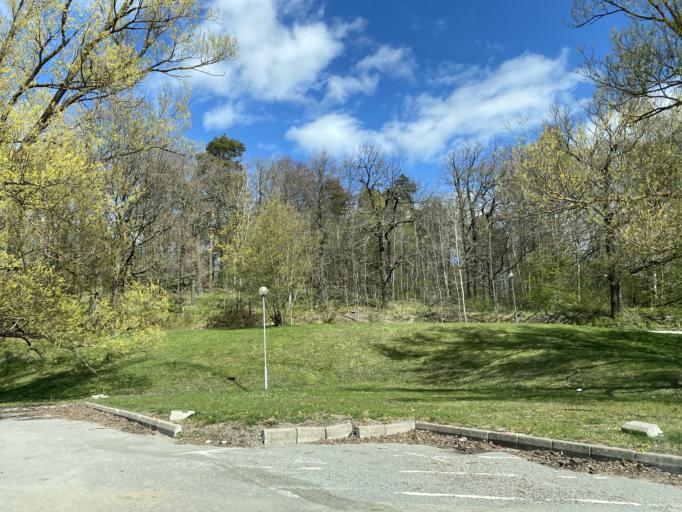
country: SE
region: Stockholm
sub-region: Stockholms Kommun
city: Stockholm
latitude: 59.3617
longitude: 18.0627
